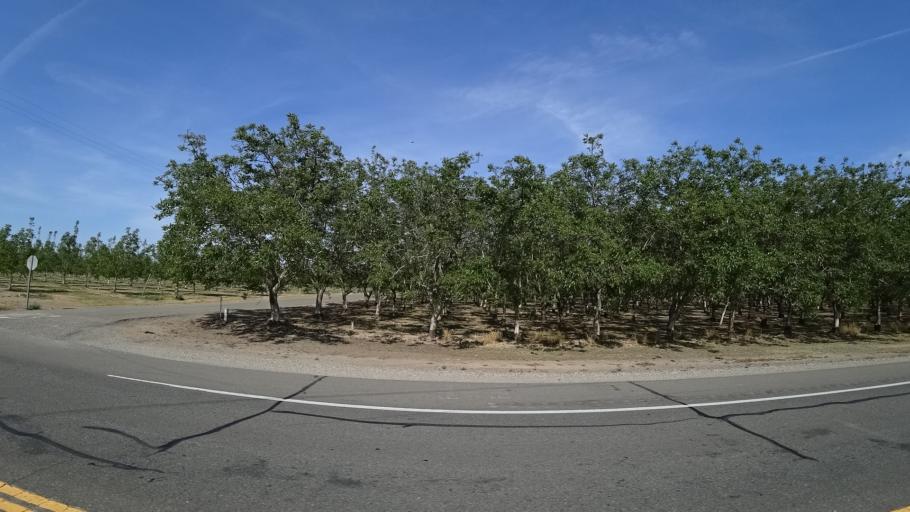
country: US
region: California
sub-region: Tehama County
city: Los Molinos
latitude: 40.0061
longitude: -122.0924
